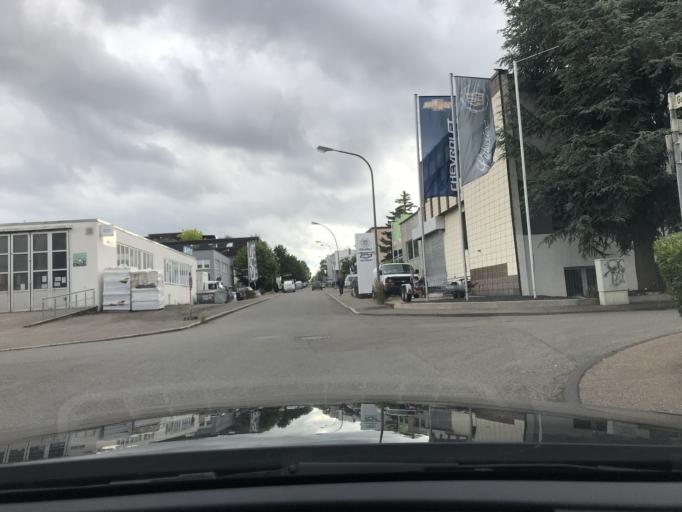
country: DE
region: Baden-Wuerttemberg
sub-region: Regierungsbezirk Stuttgart
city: Fellbach
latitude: 48.8296
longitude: 9.2597
